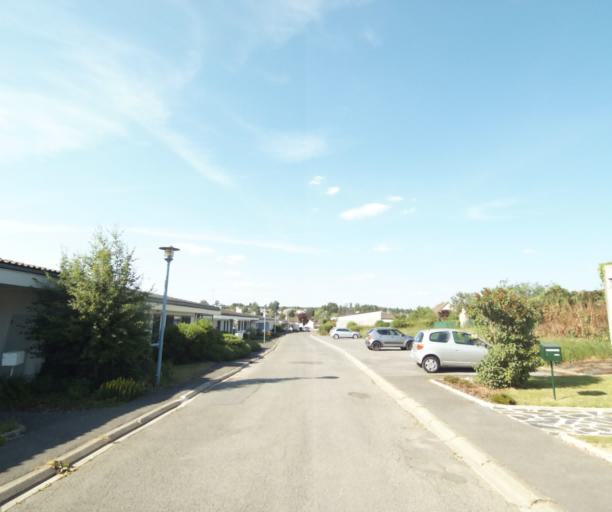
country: FR
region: Champagne-Ardenne
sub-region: Departement des Ardennes
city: Warcq
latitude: 49.7790
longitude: 4.6977
